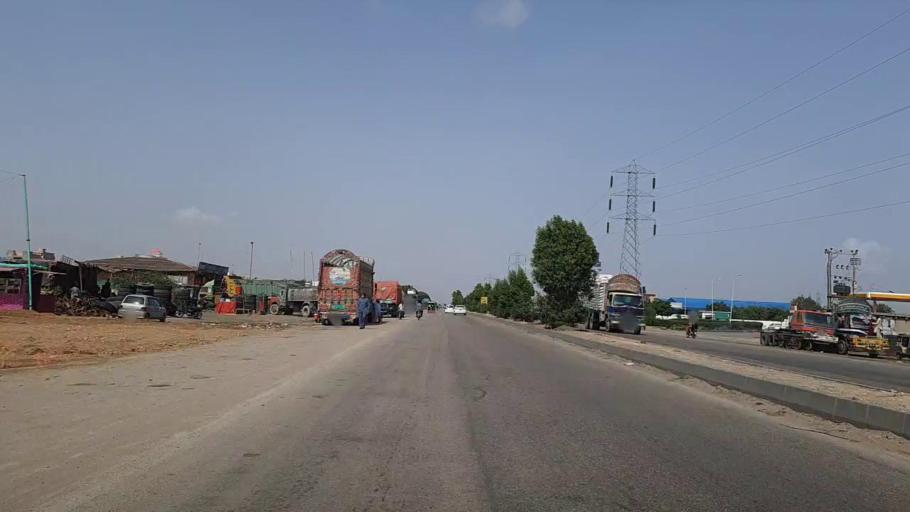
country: PK
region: Sindh
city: Malir Cantonment
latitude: 24.8616
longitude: 67.3514
